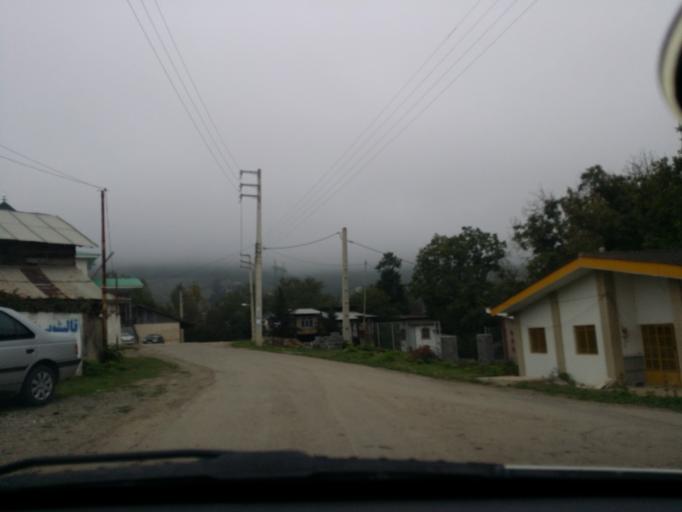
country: IR
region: Mazandaran
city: Chalus
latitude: 36.5103
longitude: 51.2268
